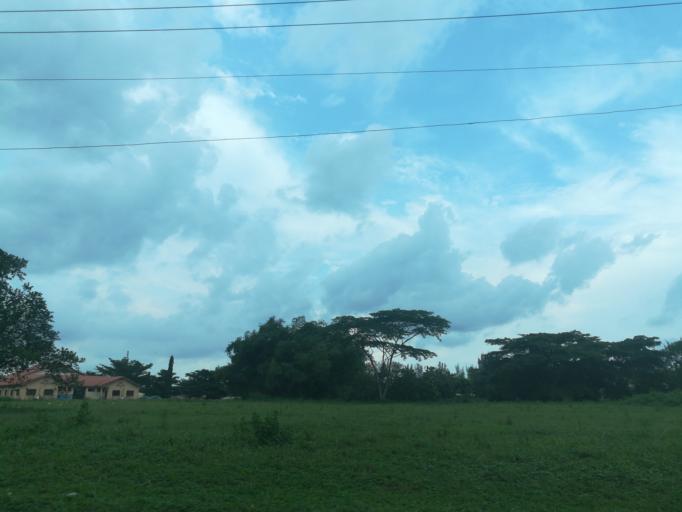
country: NG
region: Lagos
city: Ikorodu
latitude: 6.6364
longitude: 3.5217
